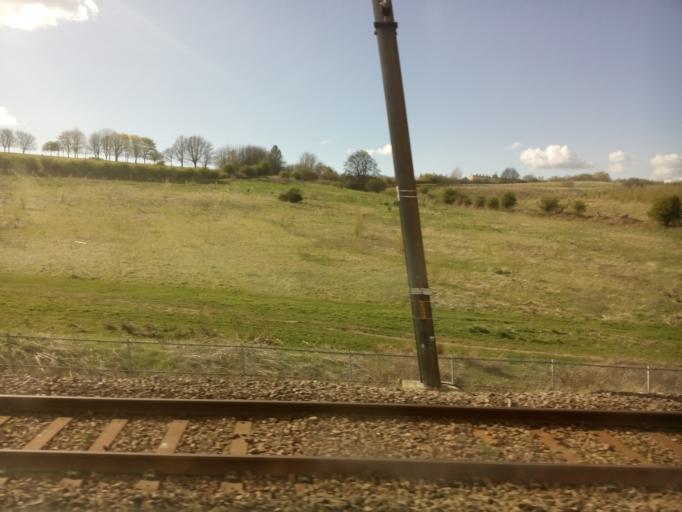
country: GB
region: England
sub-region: County Durham
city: Durham
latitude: 54.7870
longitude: -1.5748
